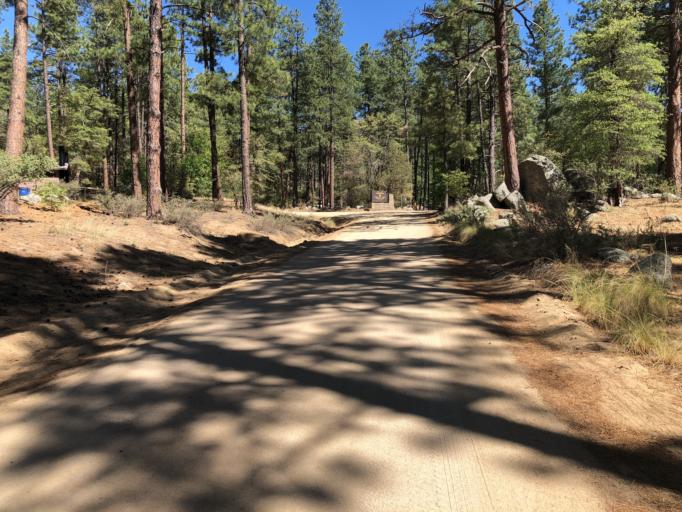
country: US
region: Arizona
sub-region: Yavapai County
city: Prescott
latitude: 34.4555
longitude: -112.4609
